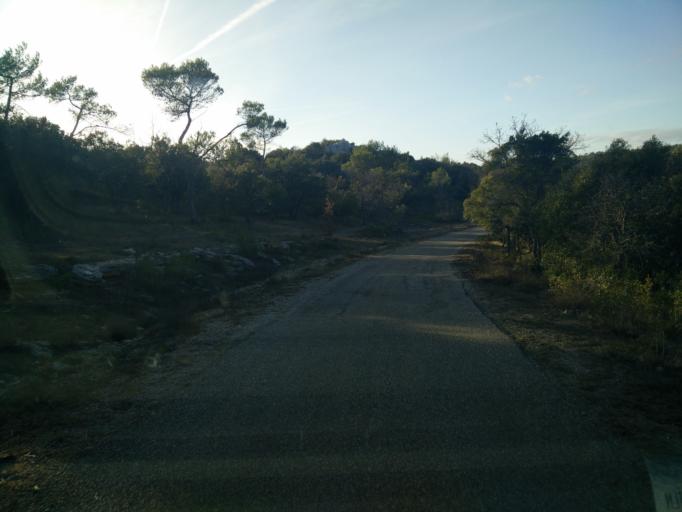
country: FR
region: Provence-Alpes-Cote d'Azur
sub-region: Departement du Var
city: Le Revest-les-Eaux
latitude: 43.2264
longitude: 5.9281
